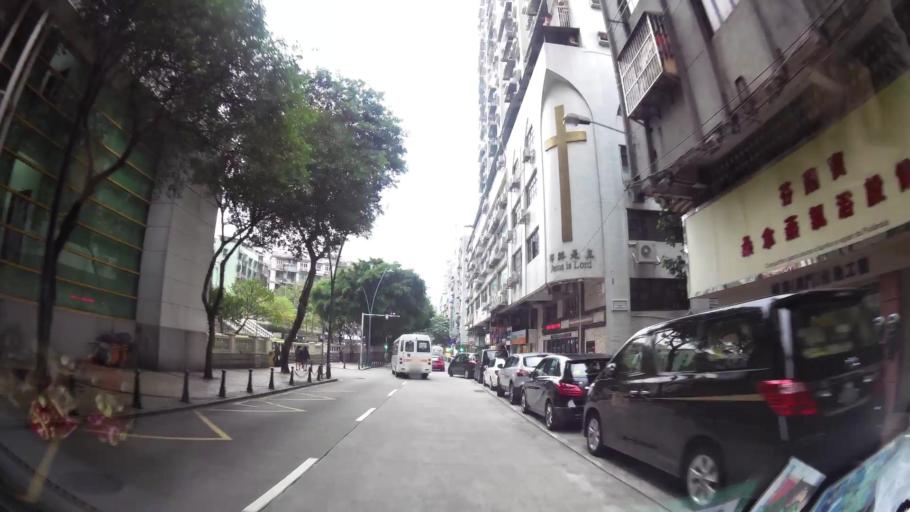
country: MO
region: Macau
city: Macau
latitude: 22.1970
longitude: 113.5466
